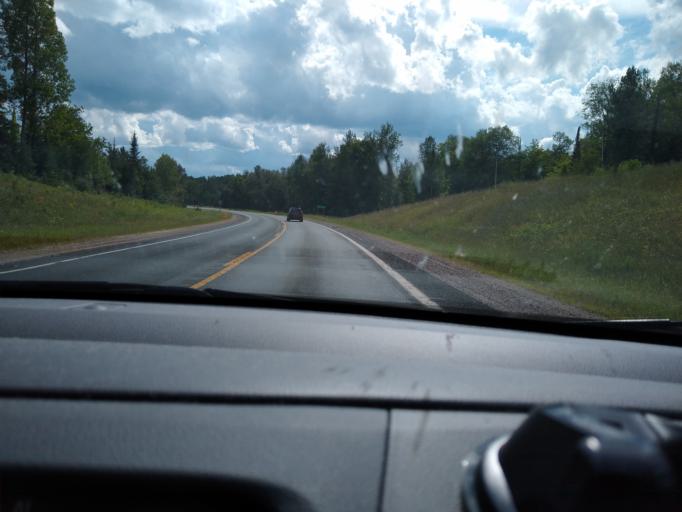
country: US
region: Michigan
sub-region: Iron County
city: Crystal Falls
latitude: 46.2833
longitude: -88.0160
